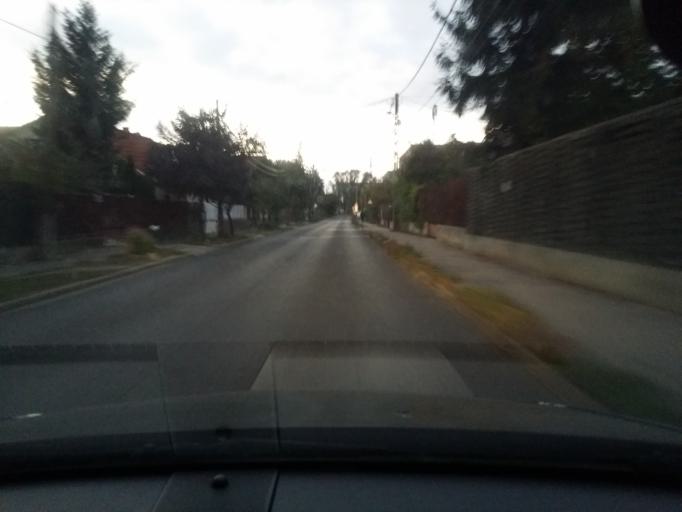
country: HU
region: Budapest
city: Budapest XVI. keruelet
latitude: 47.5249
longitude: 19.1495
